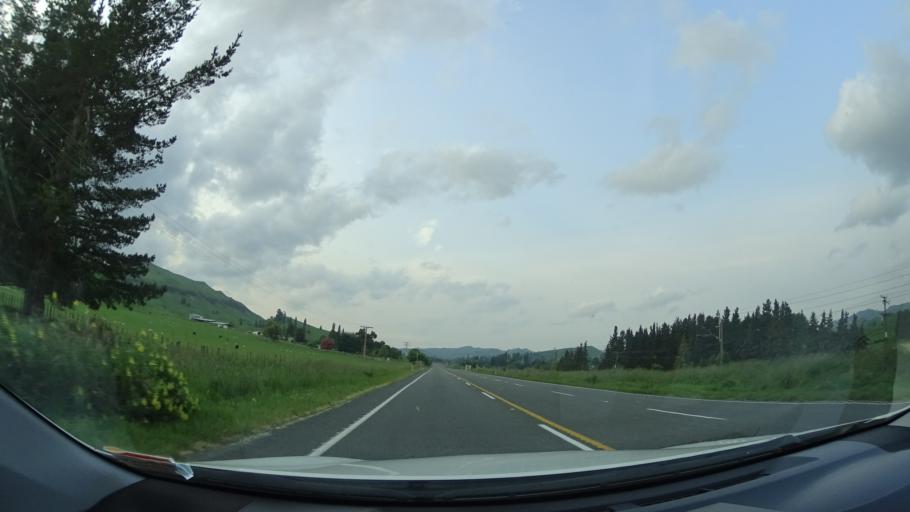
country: NZ
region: Manawatu-Wanganui
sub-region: Ruapehu District
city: Waiouru
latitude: -39.7262
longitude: 175.8422
